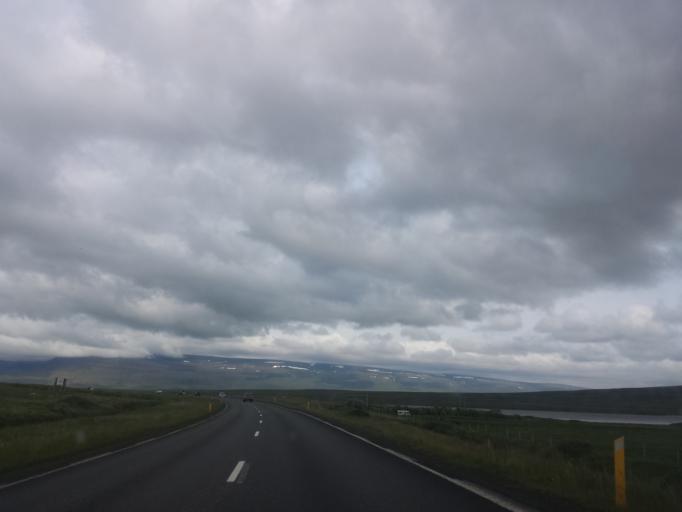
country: IS
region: Northwest
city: Saudarkrokur
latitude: 65.3446
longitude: -20.7872
